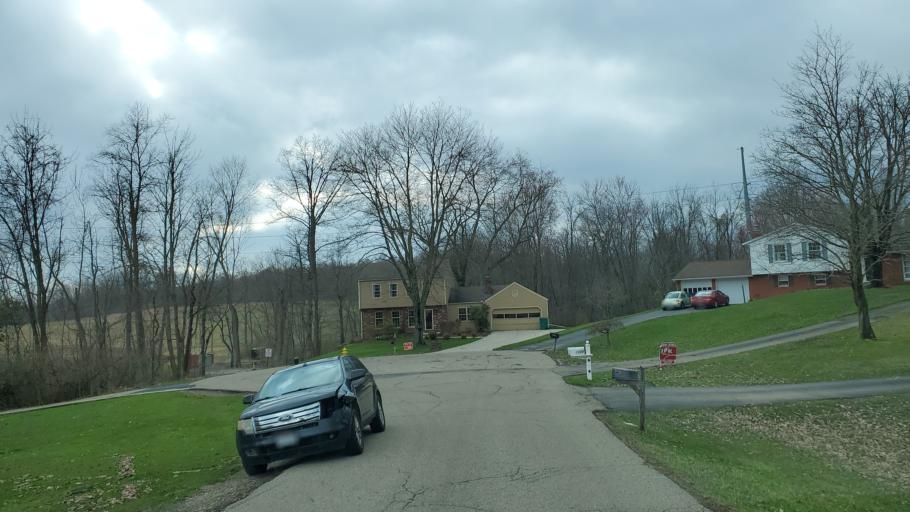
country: US
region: Ohio
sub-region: Licking County
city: Newark
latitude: 40.0300
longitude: -82.3816
